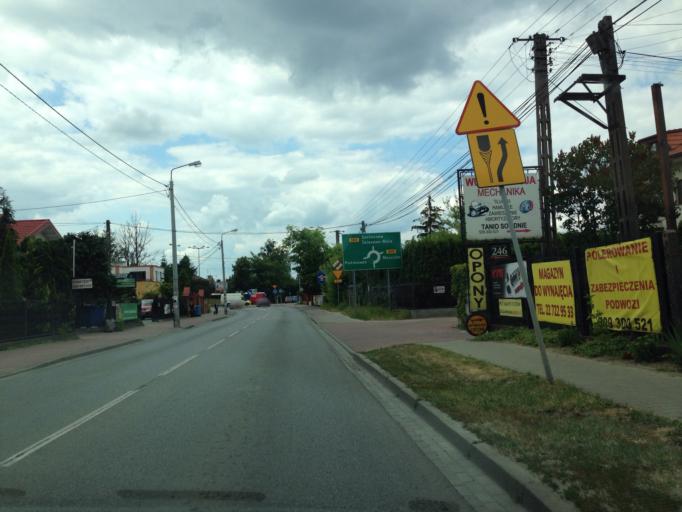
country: PL
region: Masovian Voivodeship
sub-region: Powiat warszawski zachodni
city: Babice
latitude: 52.2474
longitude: 20.8492
